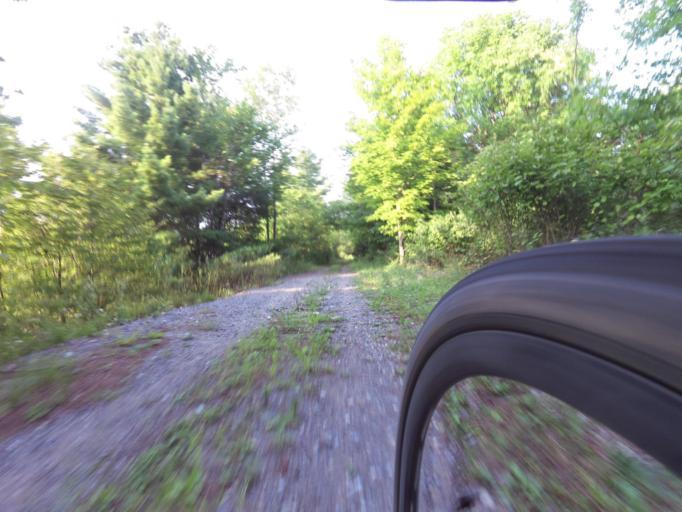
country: CA
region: Ontario
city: Gananoque
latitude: 44.5722
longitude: -76.3450
